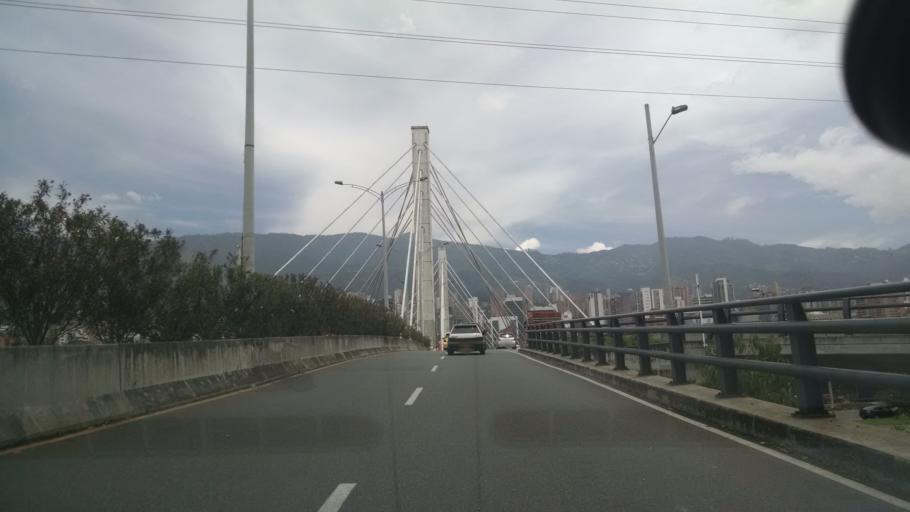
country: CO
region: Antioquia
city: Itagui
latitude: 6.2044
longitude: -75.5806
